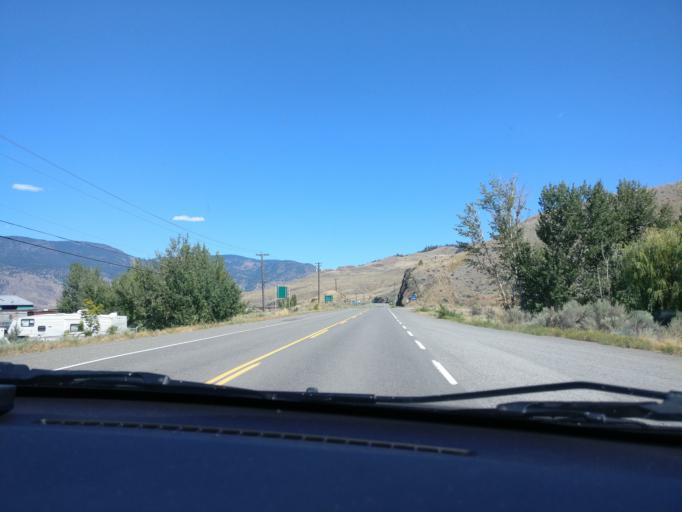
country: CA
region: British Columbia
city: Logan Lake
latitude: 50.7595
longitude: -120.8099
